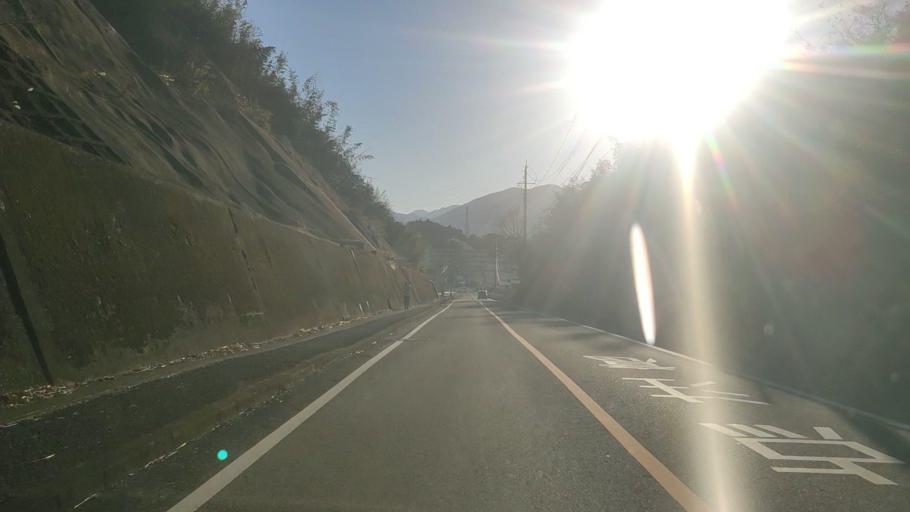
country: JP
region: Miyazaki
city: Miyazaki-shi
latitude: 31.8644
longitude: 131.3884
